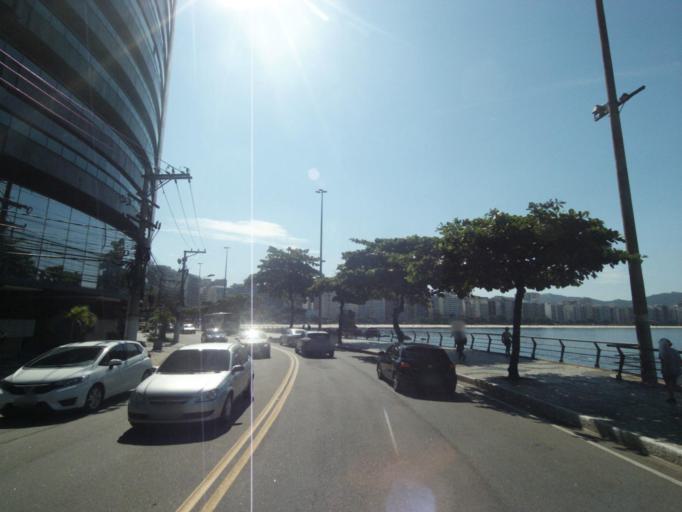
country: BR
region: Rio de Janeiro
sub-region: Niteroi
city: Niteroi
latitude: -22.9053
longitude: -43.1196
